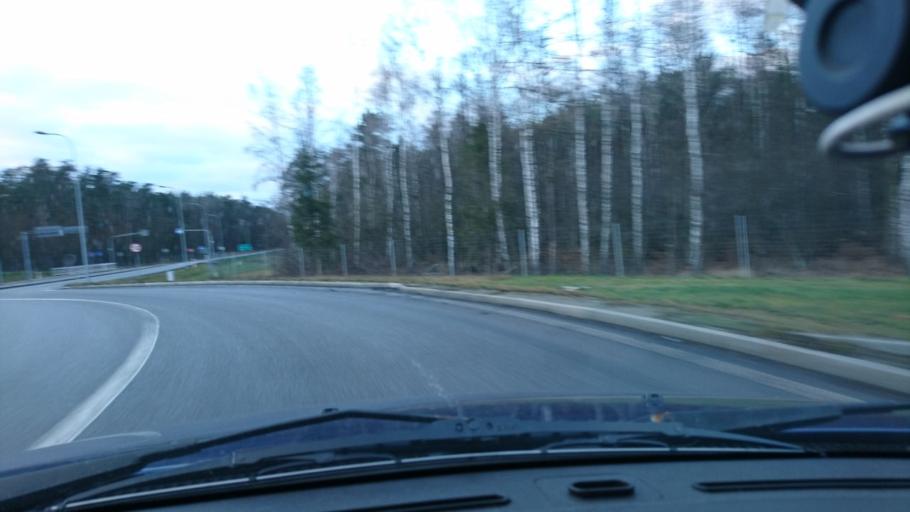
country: PL
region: Greater Poland Voivodeship
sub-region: Powiat kepinski
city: Kepno
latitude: 51.3314
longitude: 17.9591
